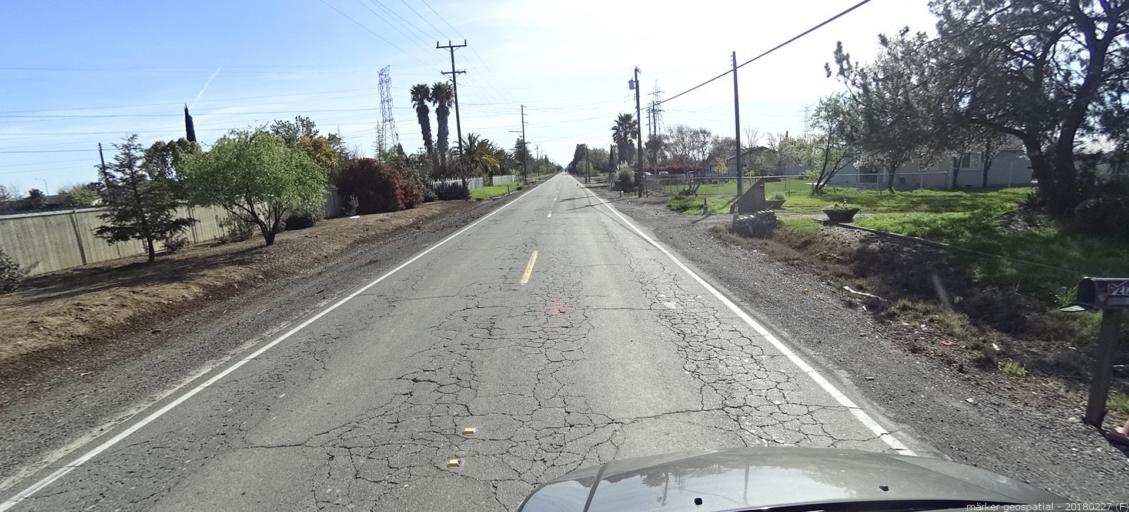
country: US
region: California
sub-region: Sacramento County
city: Rosemont
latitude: 38.5108
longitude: -121.3576
